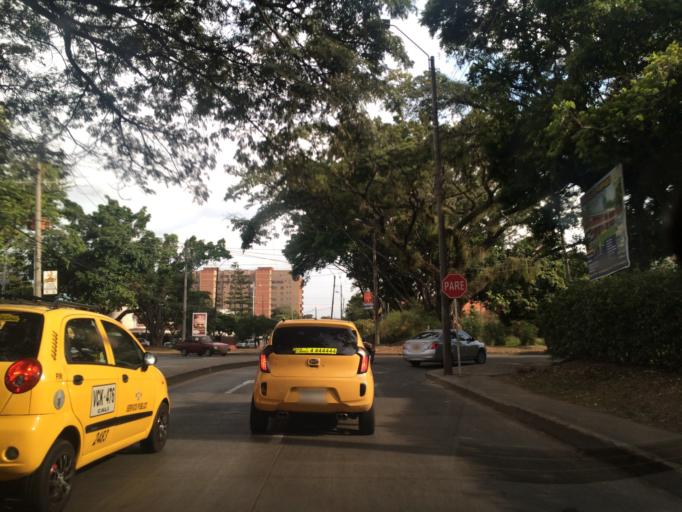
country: CO
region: Valle del Cauca
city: Cali
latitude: 3.4106
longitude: -76.5557
